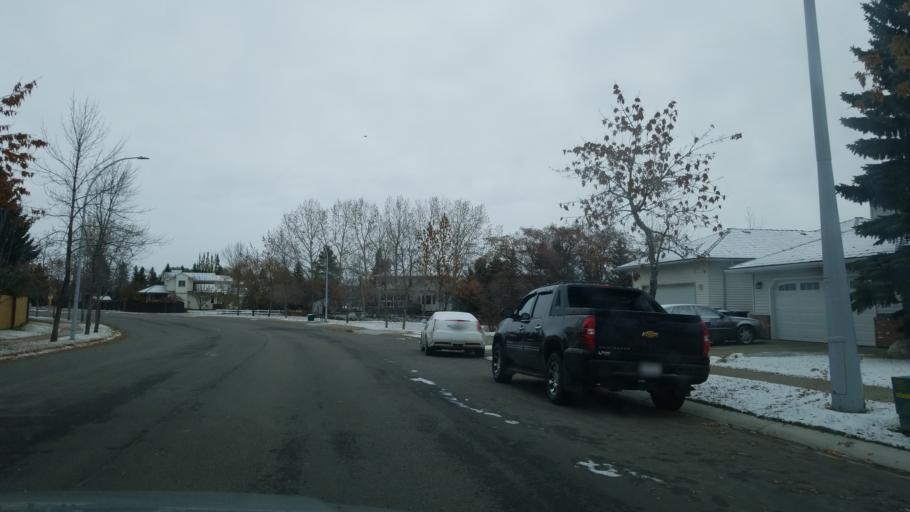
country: CA
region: Alberta
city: Sherwood Park
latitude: 53.5230
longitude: -113.2759
